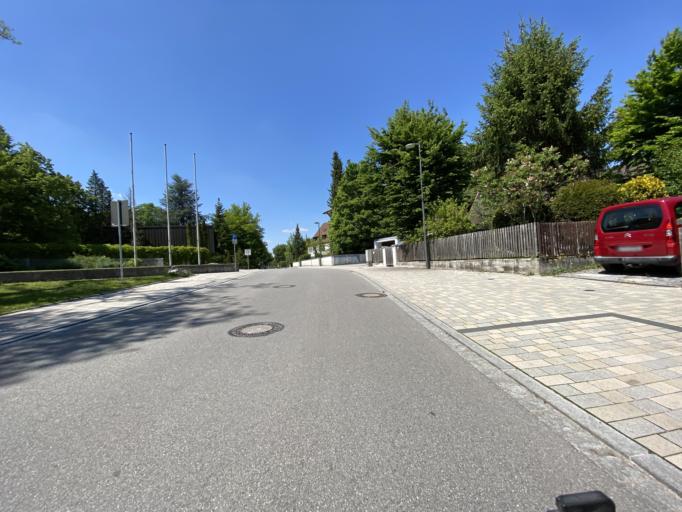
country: DE
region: Bavaria
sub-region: Upper Bavaria
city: Grafelfing
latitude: 48.1212
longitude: 11.4258
